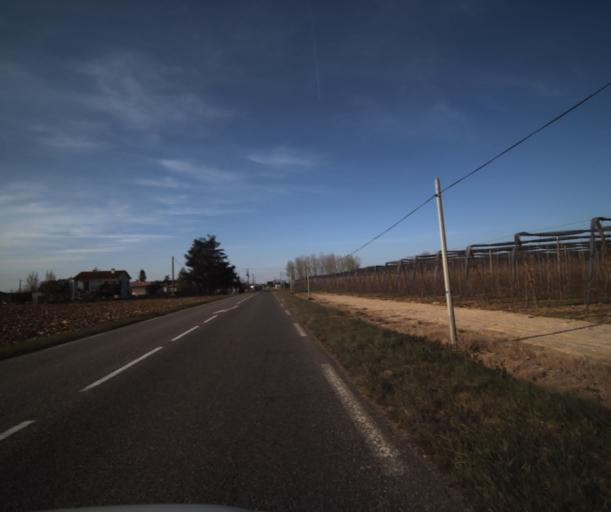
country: FR
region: Midi-Pyrenees
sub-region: Departement du Tarn-et-Garonne
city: Corbarieu
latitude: 43.9363
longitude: 1.3592
